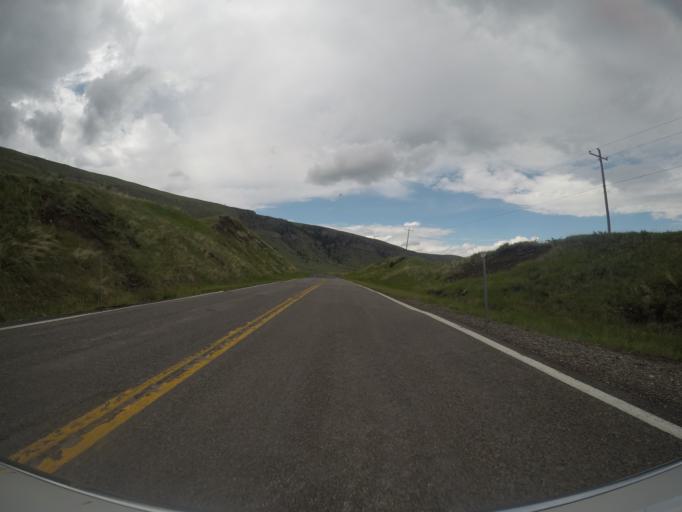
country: US
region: Montana
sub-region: Sweet Grass County
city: Big Timber
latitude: 45.5663
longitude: -110.2017
